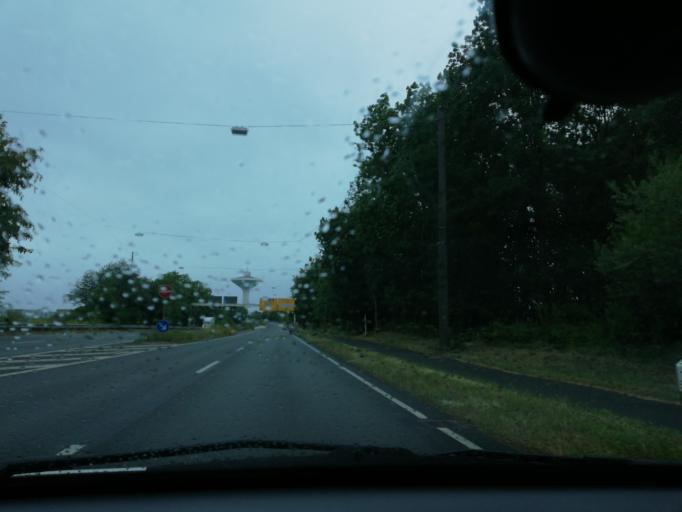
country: DE
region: North Rhine-Westphalia
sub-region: Regierungsbezirk Dusseldorf
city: Wuppertal
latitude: 51.2397
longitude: 7.1933
